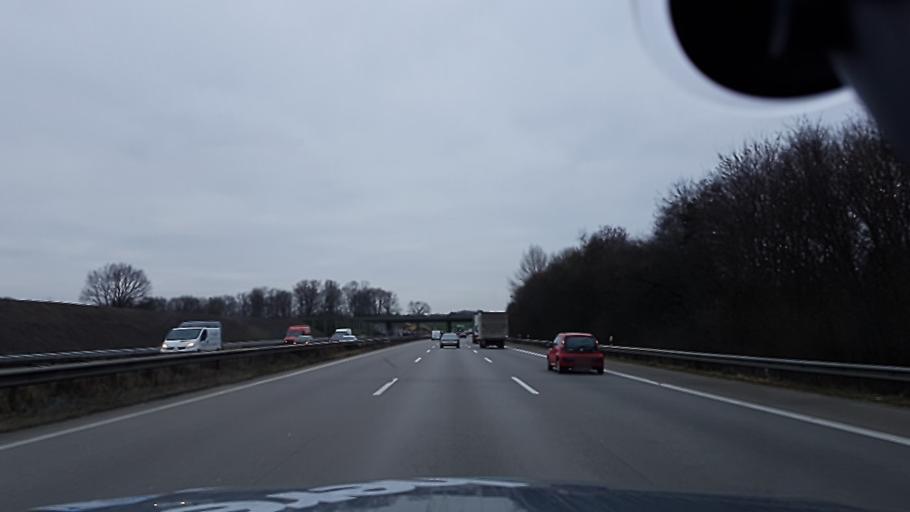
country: DE
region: Schleswig-Holstein
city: Barsbuettel
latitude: 53.5697
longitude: 10.1921
